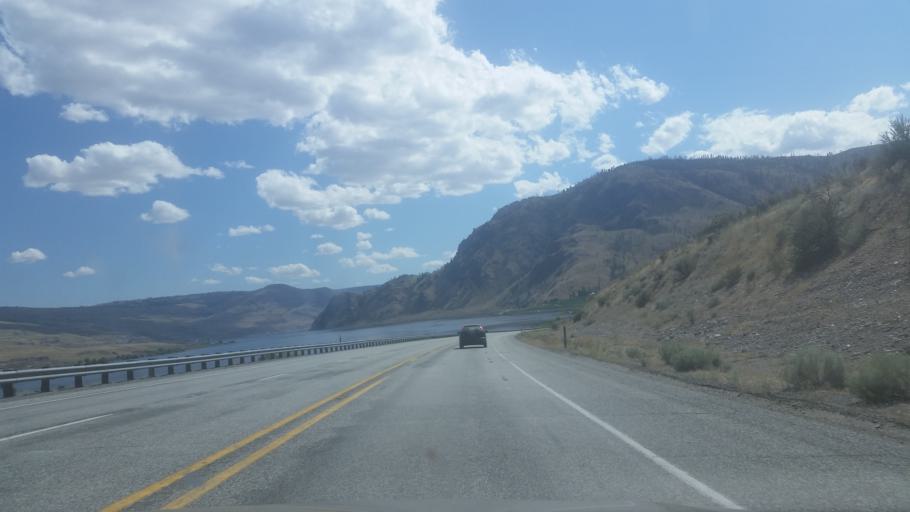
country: US
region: Washington
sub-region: Okanogan County
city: Brewster
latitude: 47.9968
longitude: -119.8837
